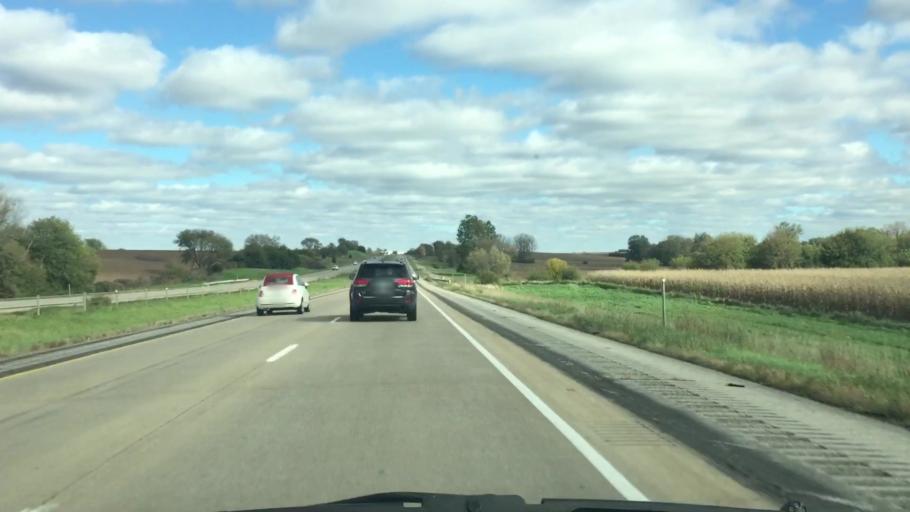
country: US
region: Iowa
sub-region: Cedar County
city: West Branch
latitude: 41.6671
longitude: -91.4123
